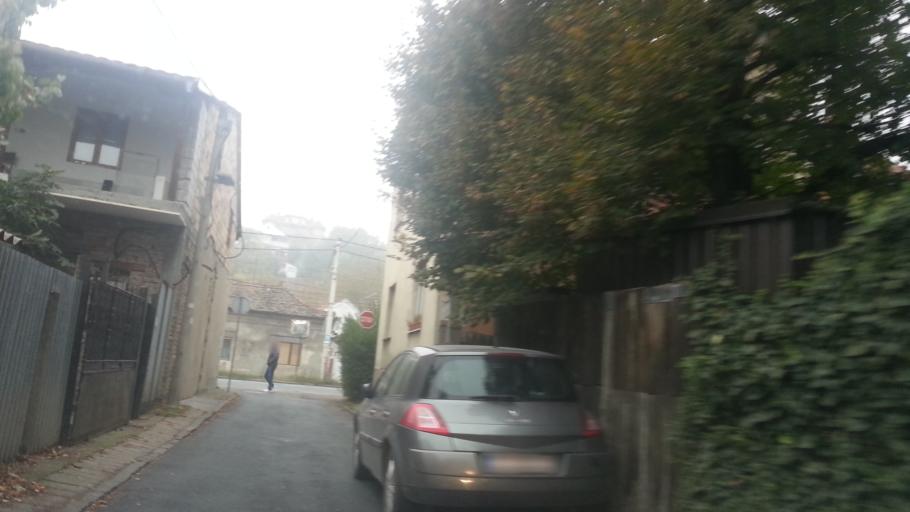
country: RS
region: Central Serbia
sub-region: Belgrade
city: Zemun
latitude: 44.8364
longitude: 20.4025
